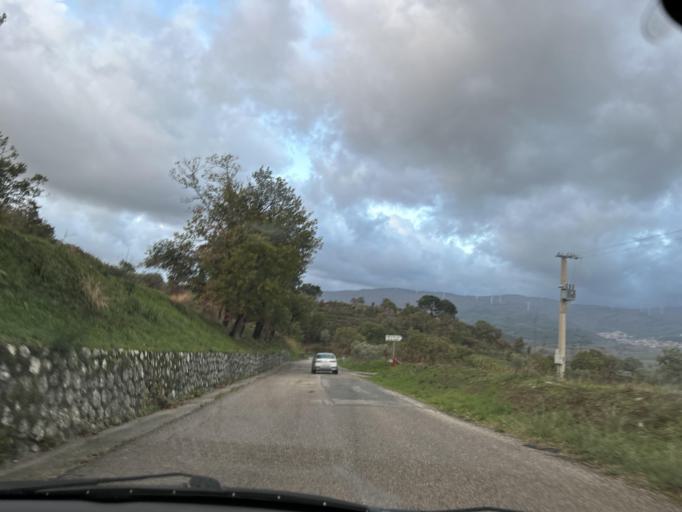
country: IT
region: Calabria
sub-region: Provincia di Catanzaro
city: Squillace
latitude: 38.7689
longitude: 16.5129
